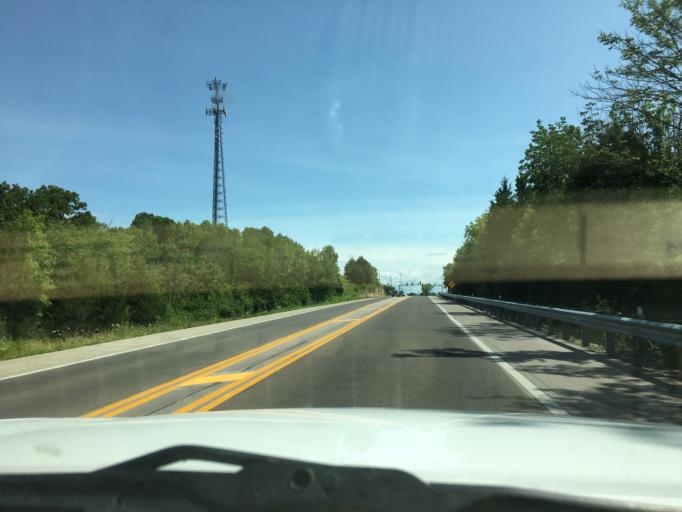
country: US
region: Missouri
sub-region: Franklin County
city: Union
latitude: 38.4848
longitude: -91.0052
